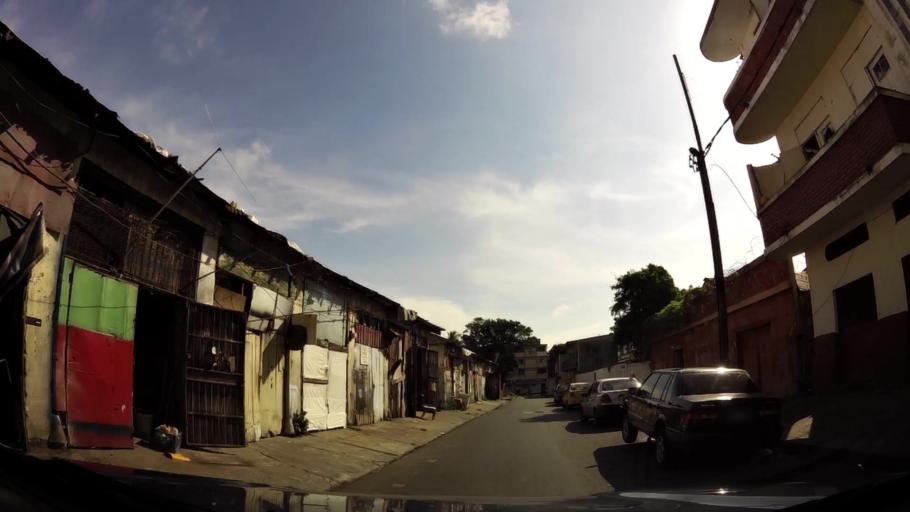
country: PA
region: Panama
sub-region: Distrito de Panama
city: Ancon
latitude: 8.9542
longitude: -79.5436
